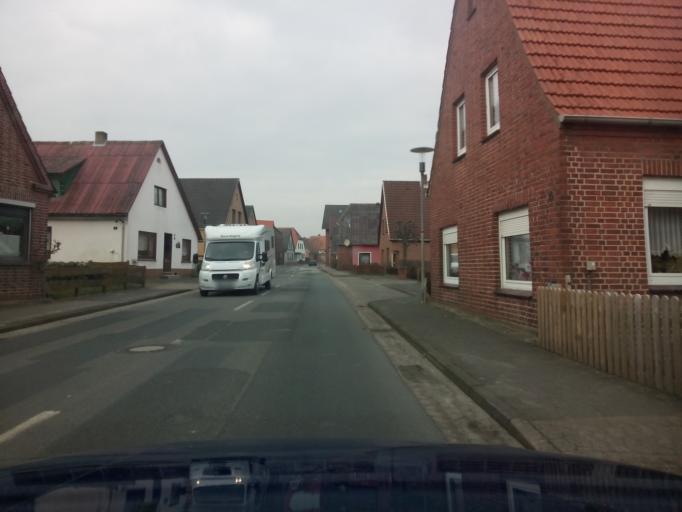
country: DE
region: Lower Saxony
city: Lintig
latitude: 53.6223
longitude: 8.8452
